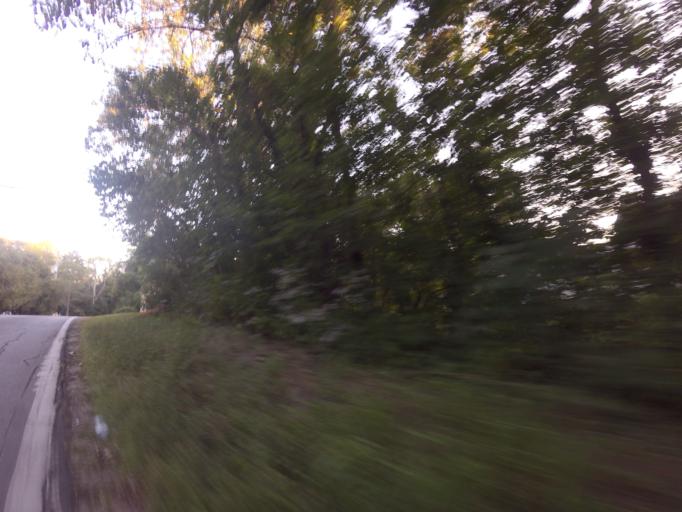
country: CA
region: Quebec
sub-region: Laurentides
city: Oka
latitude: 45.4460
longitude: -74.1074
